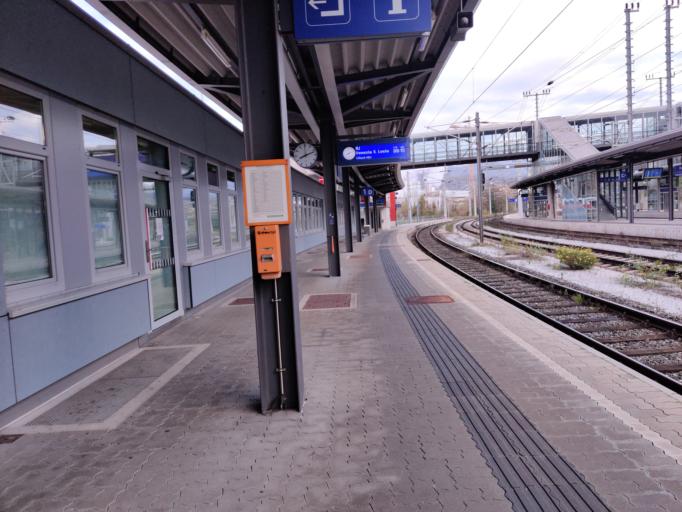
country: AT
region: Styria
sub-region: Politischer Bezirk Bruck-Muerzzuschlag
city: Bruck an der Mur
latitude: 47.4138
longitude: 15.2791
